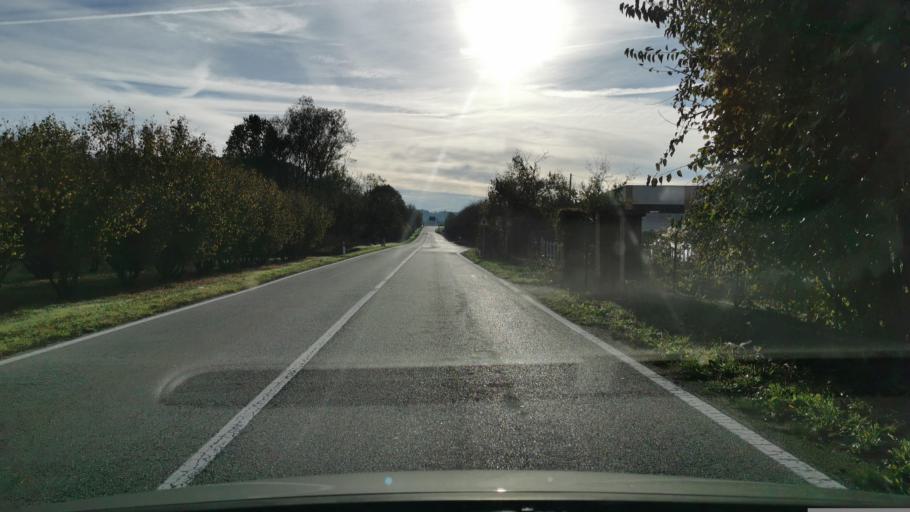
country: IT
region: Piedmont
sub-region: Provincia di Cuneo
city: Novello
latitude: 44.5879
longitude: 7.8970
